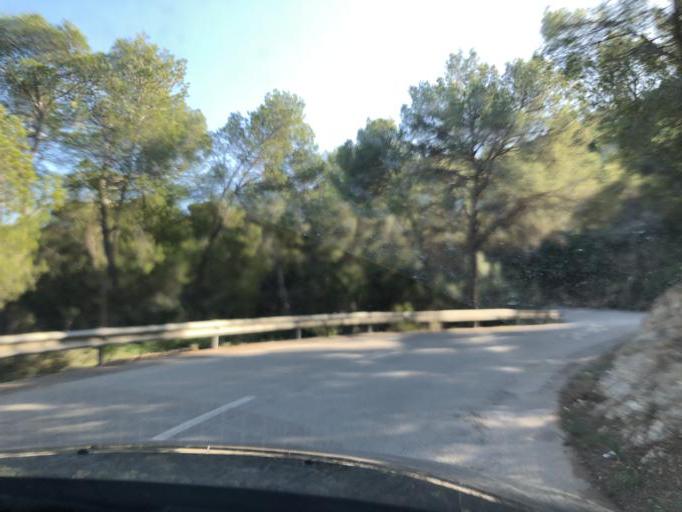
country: ES
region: Balearic Islands
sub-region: Illes Balears
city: Camp de Mar
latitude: 39.5414
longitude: 2.4021
